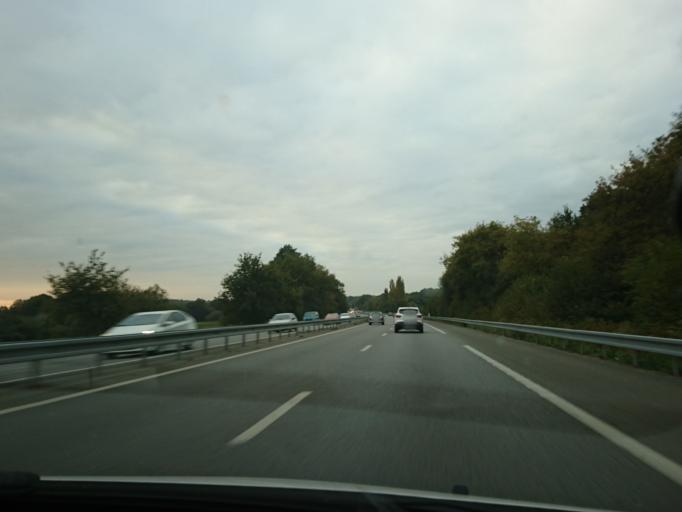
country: FR
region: Brittany
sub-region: Departement du Morbihan
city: Landevant
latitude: 47.7632
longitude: -3.1424
